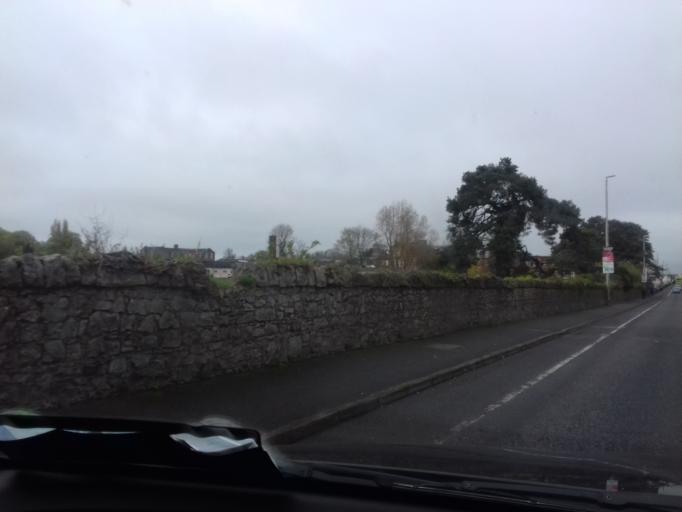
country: IE
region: Leinster
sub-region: Laois
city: Portlaoise
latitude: 53.0378
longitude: -7.2810
